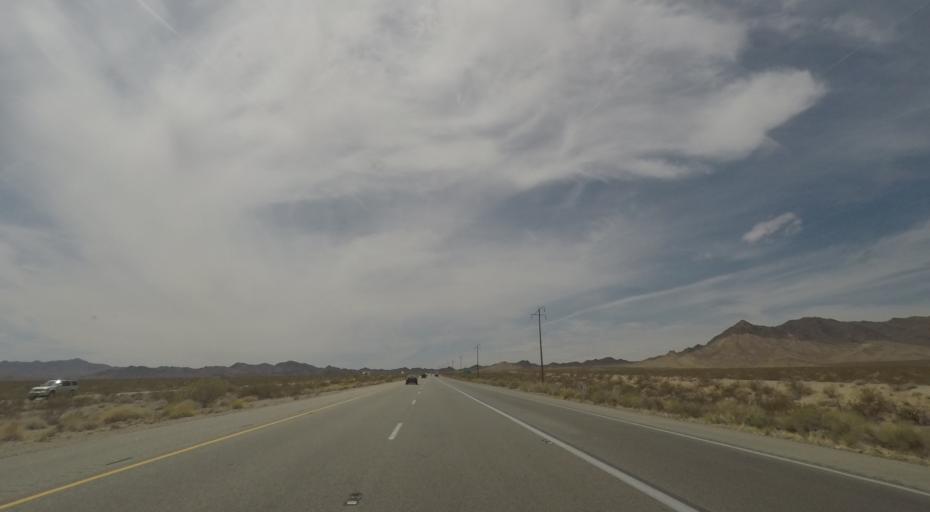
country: US
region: California
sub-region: San Bernardino County
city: Needles
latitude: 34.8387
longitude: -114.9944
